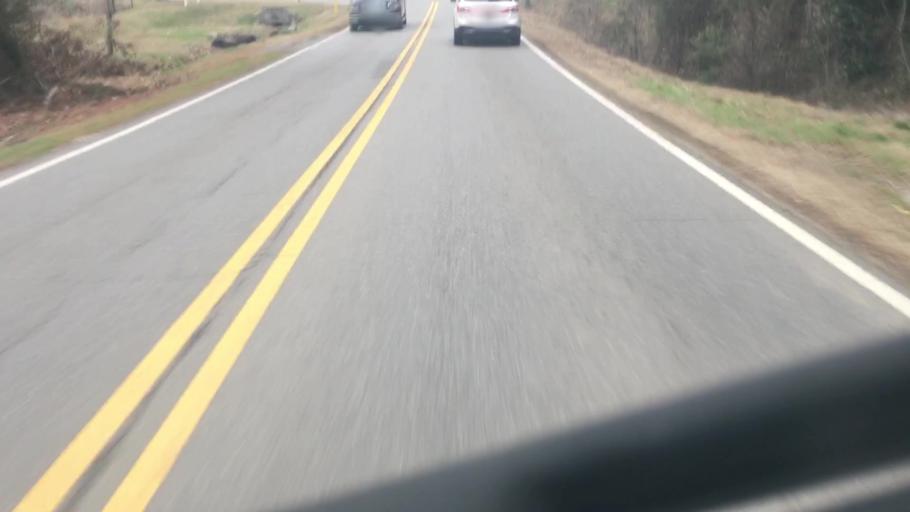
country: US
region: Alabama
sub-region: Jefferson County
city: Hoover
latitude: 33.3679
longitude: -86.8112
